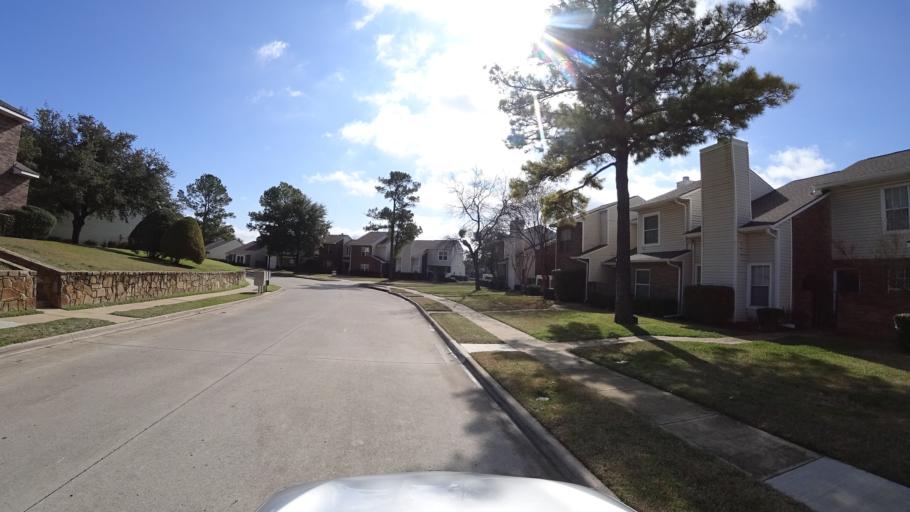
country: US
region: Texas
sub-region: Denton County
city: Lewisville
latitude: 33.0347
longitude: -97.0049
